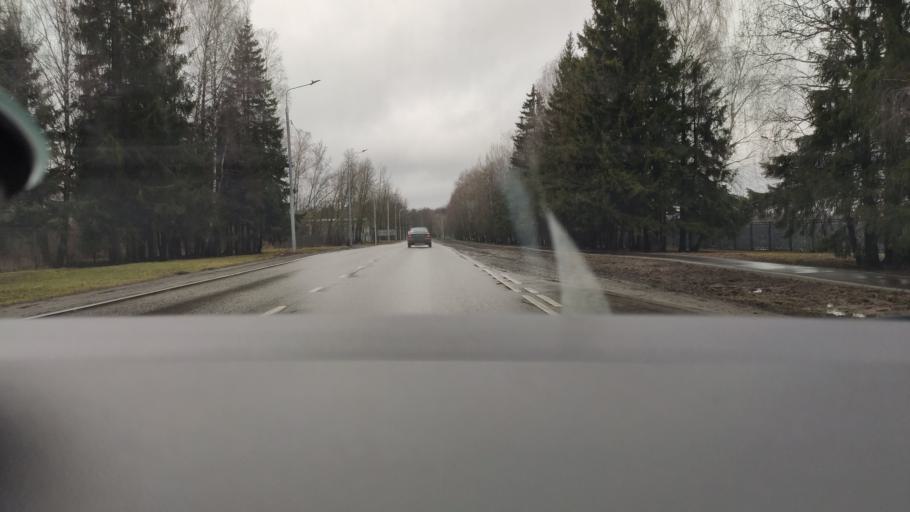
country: RU
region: Moskovskaya
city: Troitsk
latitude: 55.3014
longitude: 37.2016
